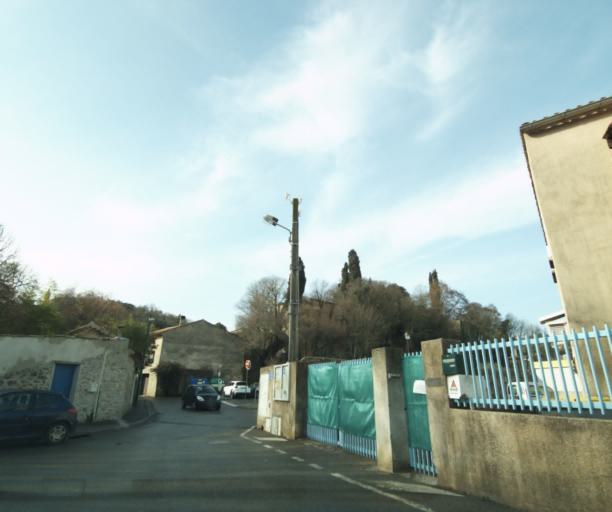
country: FR
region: Provence-Alpes-Cote d'Azur
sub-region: Departement du Var
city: Tourves
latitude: 43.4066
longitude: 5.9242
